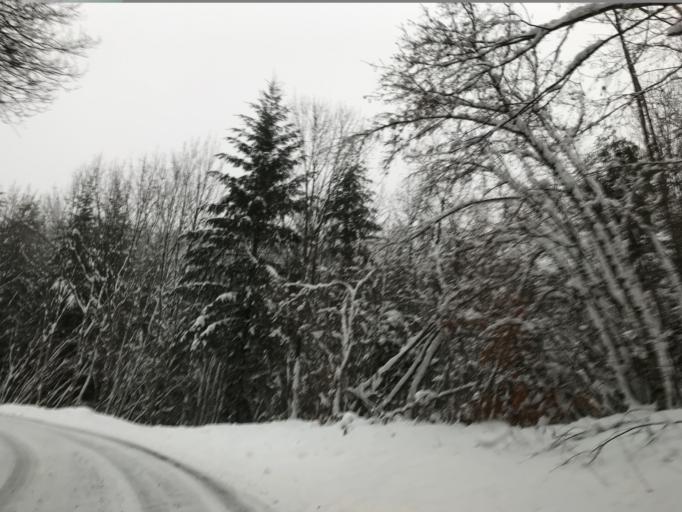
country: FR
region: Auvergne
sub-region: Departement du Puy-de-Dome
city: Job
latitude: 45.7220
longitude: 3.6967
